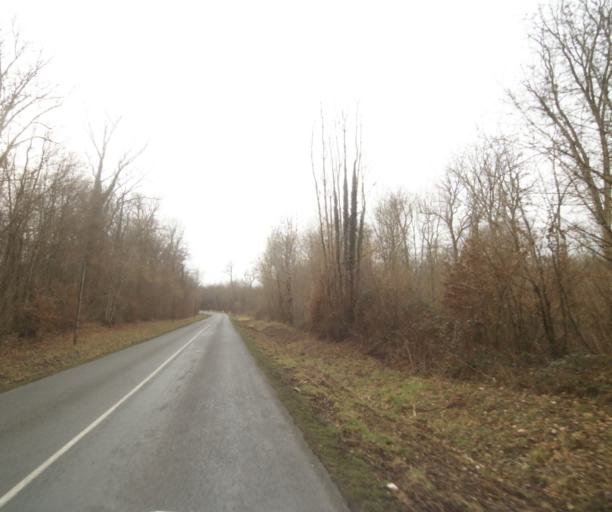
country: FR
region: Champagne-Ardenne
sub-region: Departement de la Haute-Marne
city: Villiers-en-Lieu
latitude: 48.6965
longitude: 4.8940
